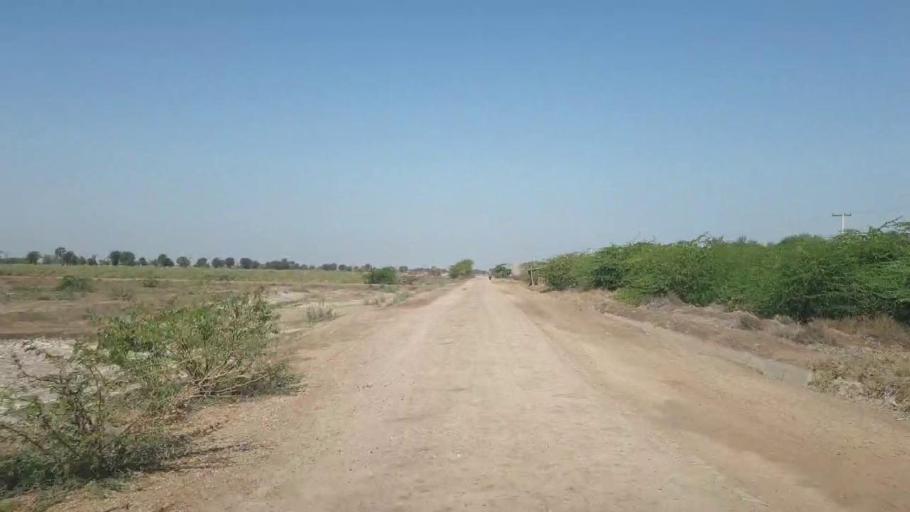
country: PK
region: Sindh
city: Umarkot
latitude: 25.3040
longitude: 69.6170
